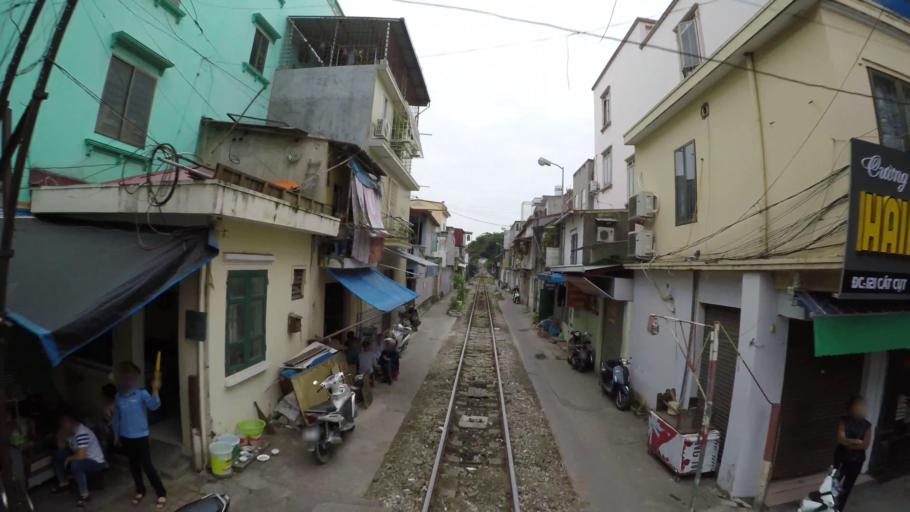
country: VN
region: Hai Phong
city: Haiphong
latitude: 20.8602
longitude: 106.6633
